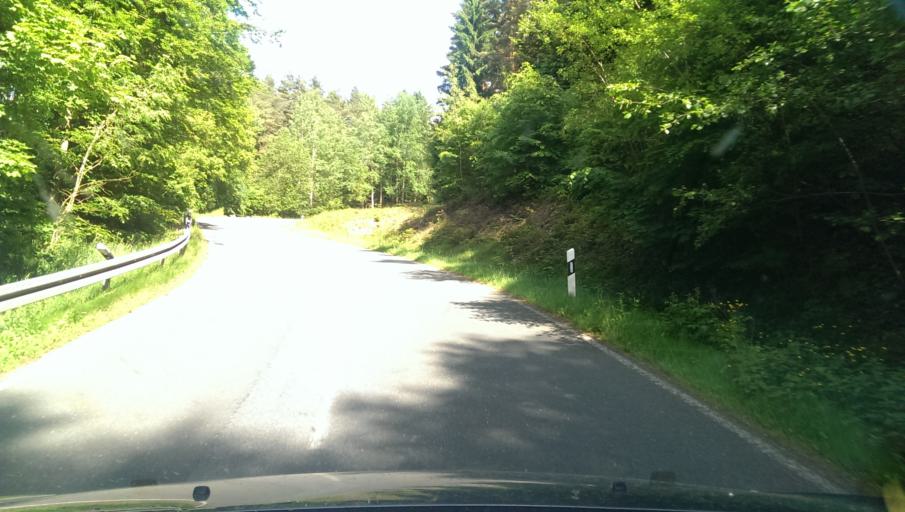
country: DE
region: Thuringia
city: Geraberg
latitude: 50.7107
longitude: 10.8301
